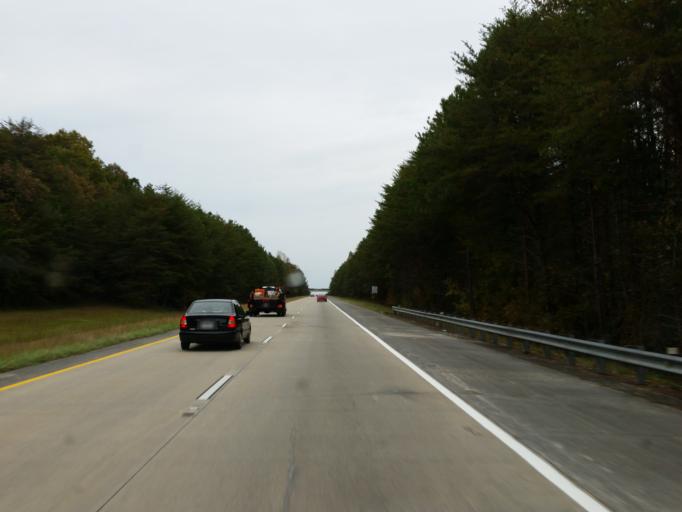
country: US
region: Georgia
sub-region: Cherokee County
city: Ball Ground
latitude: 34.3530
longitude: -84.3893
